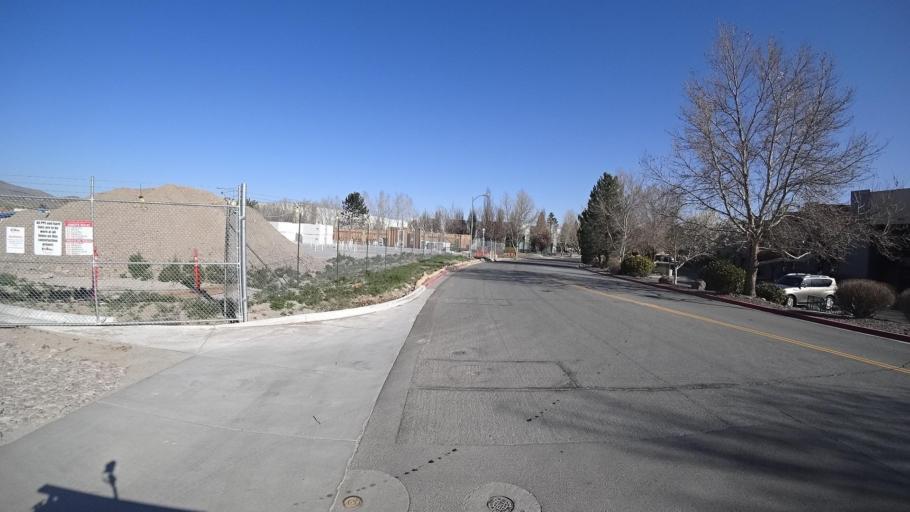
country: US
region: Nevada
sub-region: Washoe County
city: Sparks
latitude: 39.4580
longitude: -119.7767
